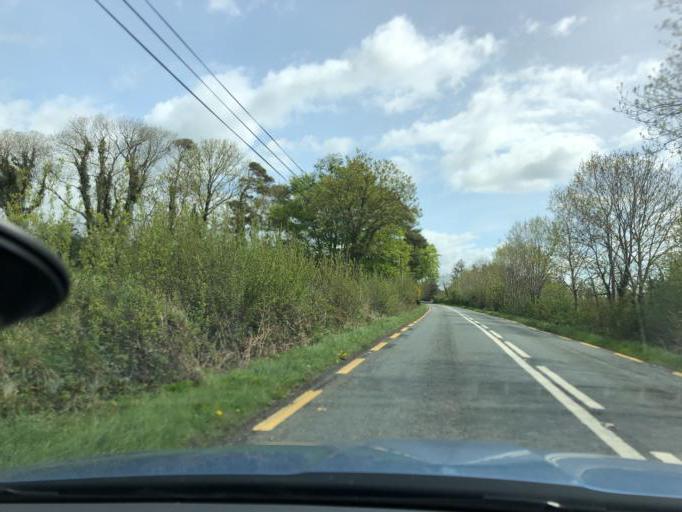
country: IE
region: Munster
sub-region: County Cork
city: Millstreet
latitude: 52.0846
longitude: -9.1807
